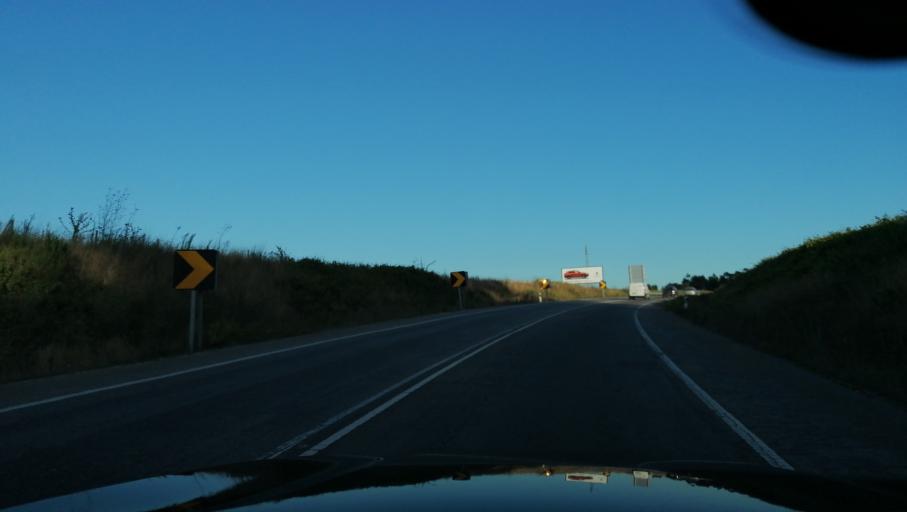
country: PT
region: Aveiro
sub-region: Aveiro
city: Aradas
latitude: 40.6102
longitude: -8.6259
